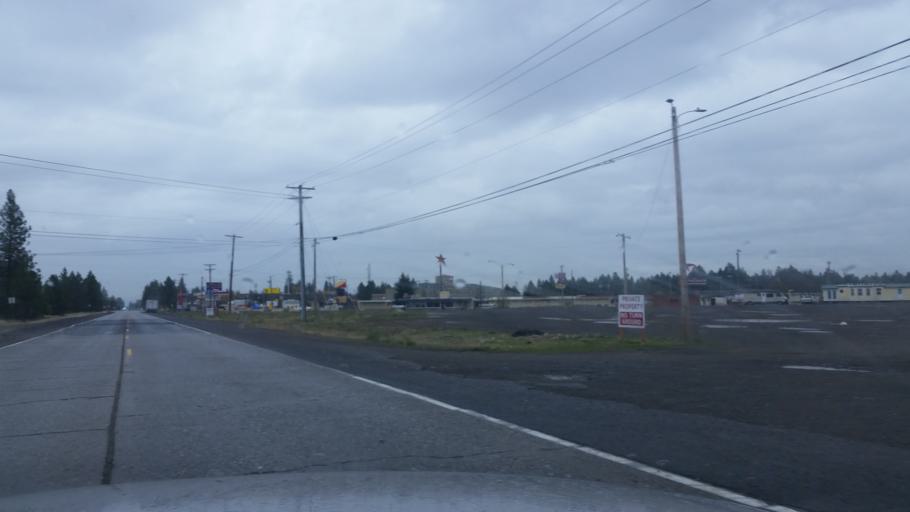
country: US
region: Washington
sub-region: Spokane County
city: Airway Heights
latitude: 47.6188
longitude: -117.5097
